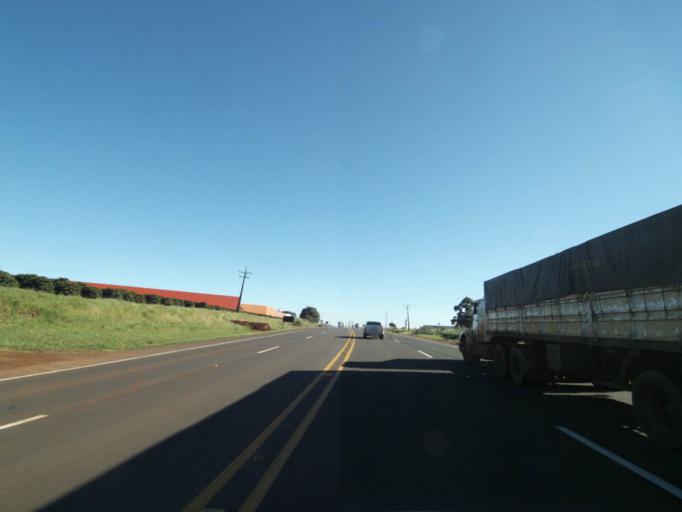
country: BR
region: Parana
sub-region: Mandaguari
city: Mandaguari
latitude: -23.5035
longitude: -51.6937
